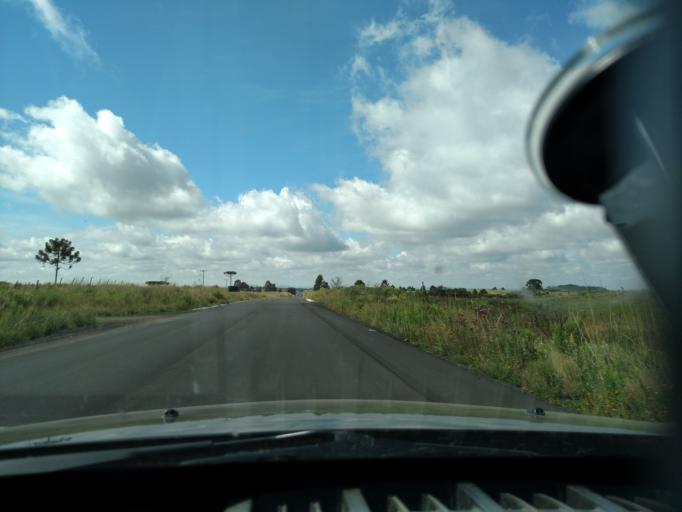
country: BR
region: Santa Catarina
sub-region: Lages
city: Lages
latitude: -27.9784
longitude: -50.0929
